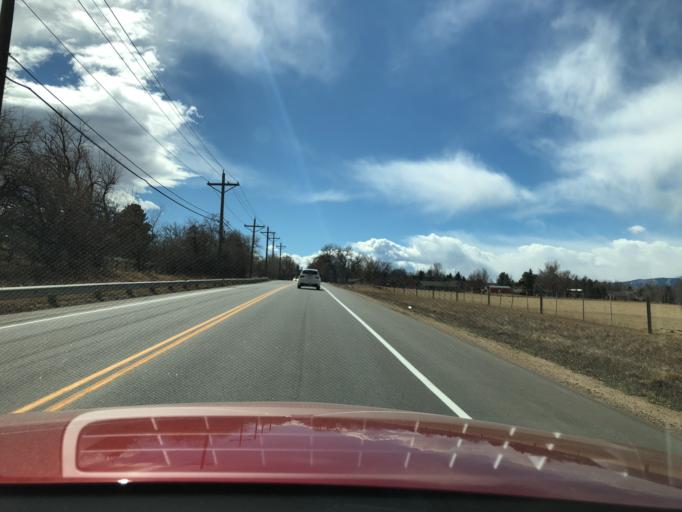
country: US
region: Colorado
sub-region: Boulder County
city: Superior
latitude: 39.9969
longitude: -105.1751
